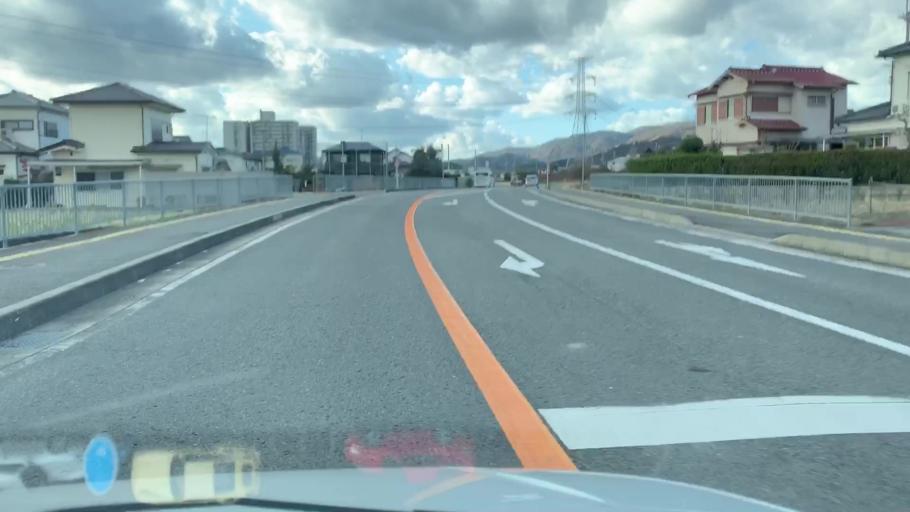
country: JP
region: Wakayama
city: Iwade
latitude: 34.2722
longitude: 135.2820
